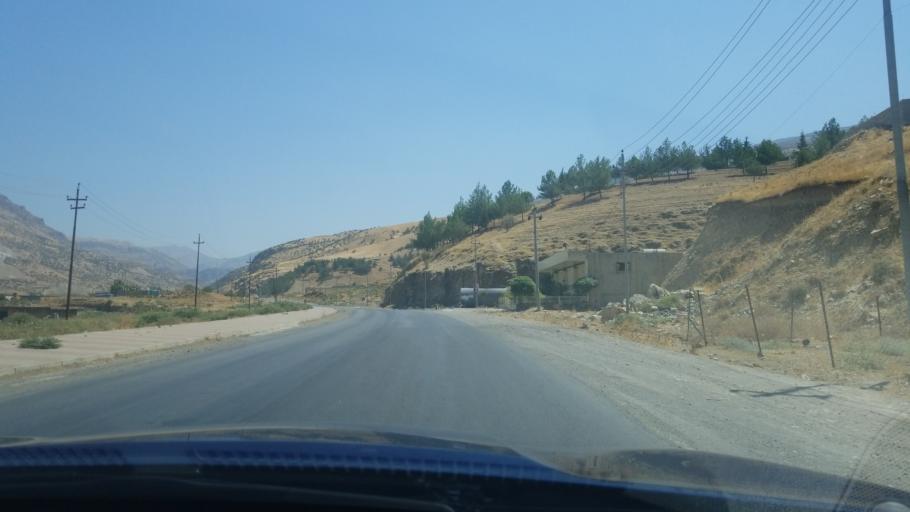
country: IQ
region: Arbil
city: Ruwandiz
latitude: 36.6212
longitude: 44.5400
